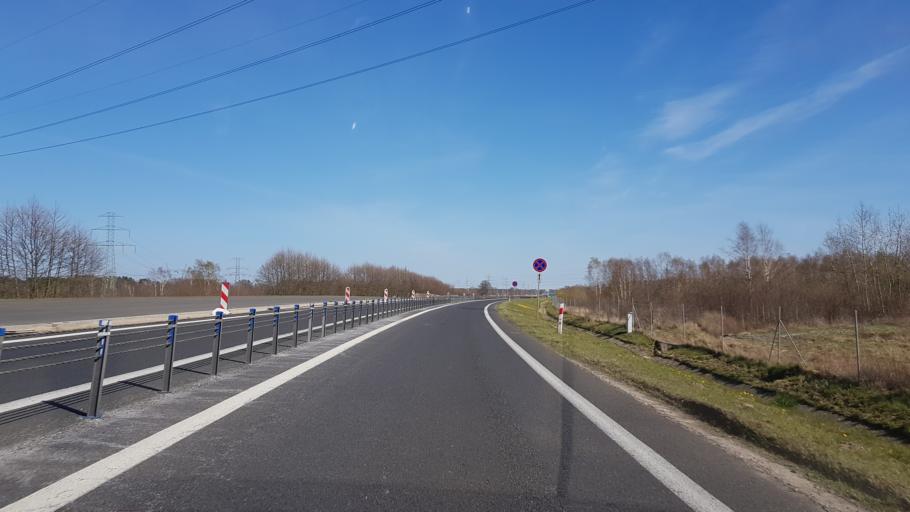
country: PL
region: West Pomeranian Voivodeship
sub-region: Powiat stargardzki
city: Kobylanka
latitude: 53.3619
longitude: 14.9019
